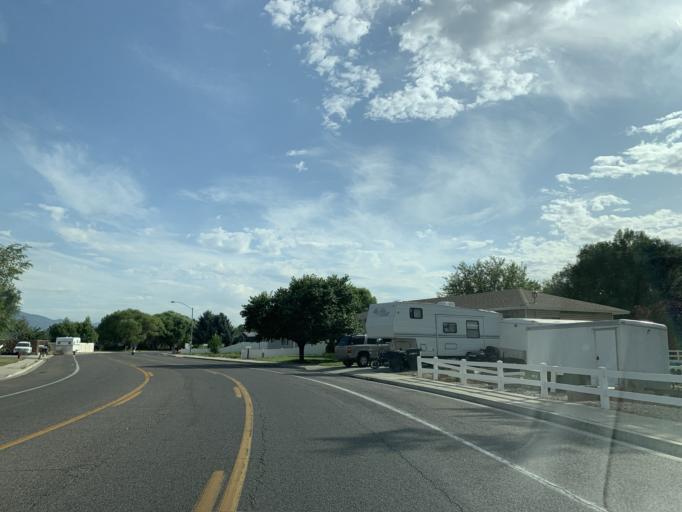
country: US
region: Utah
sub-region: Utah County
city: Provo
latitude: 40.2200
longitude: -111.6720
